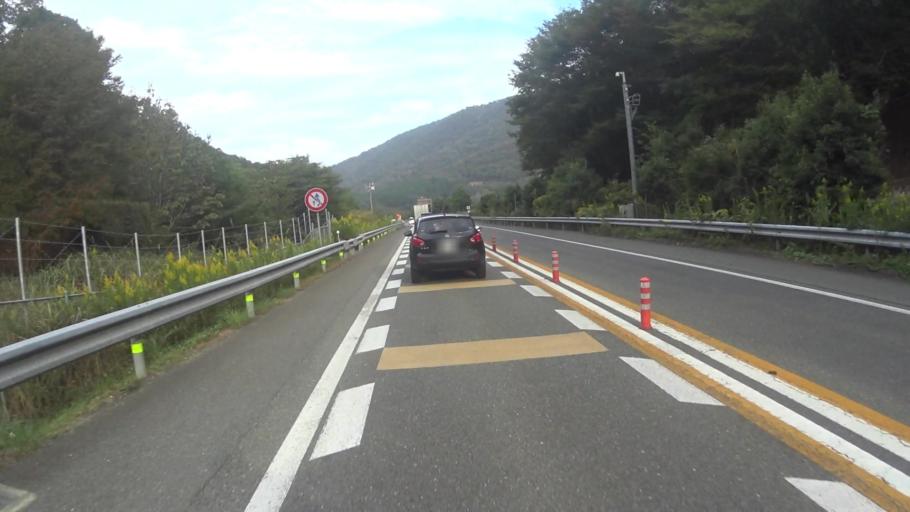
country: JP
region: Kyoto
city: Kameoka
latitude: 35.1417
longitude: 135.4446
